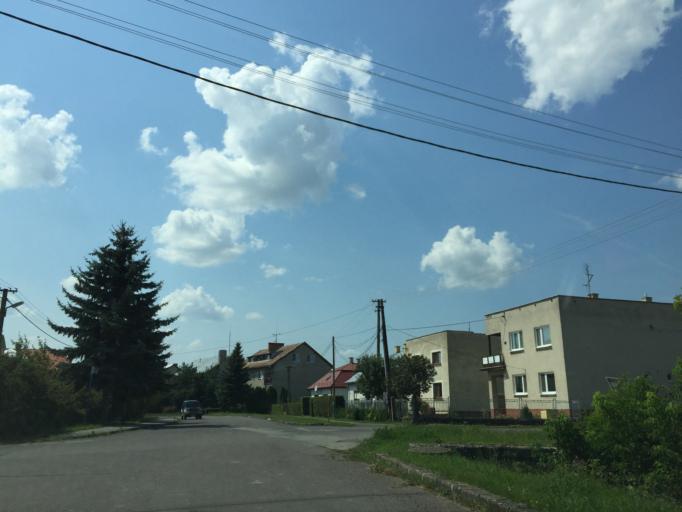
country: SK
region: Kosicky
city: Sobrance
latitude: 48.7424
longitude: 22.1864
